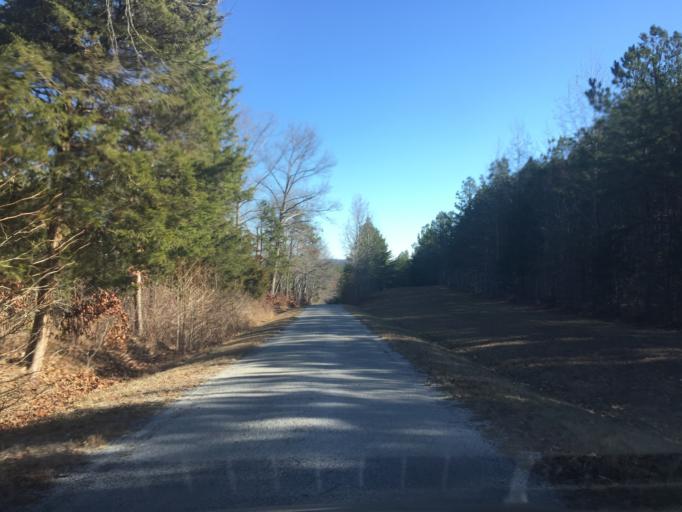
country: US
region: Tennessee
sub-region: Hamilton County
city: Harrison
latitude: 35.0889
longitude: -85.1012
